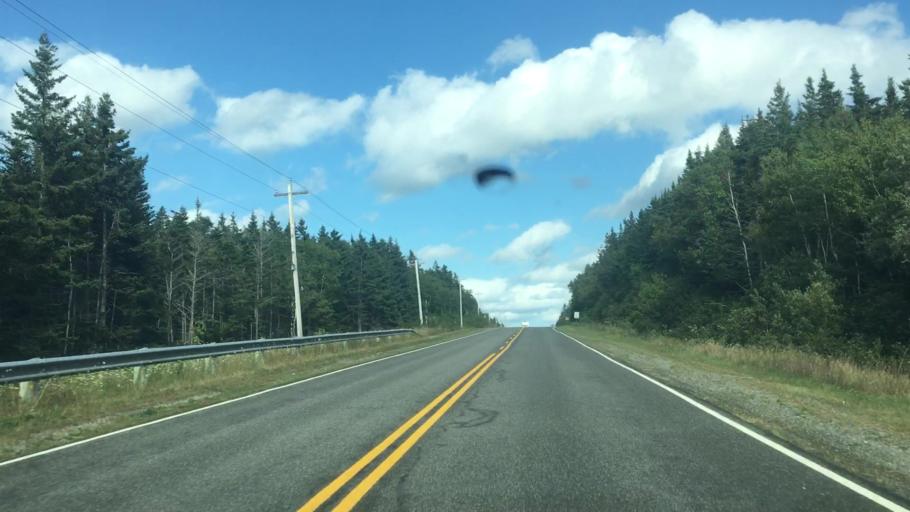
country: CA
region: Nova Scotia
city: Princeville
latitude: 45.8127
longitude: -60.7021
